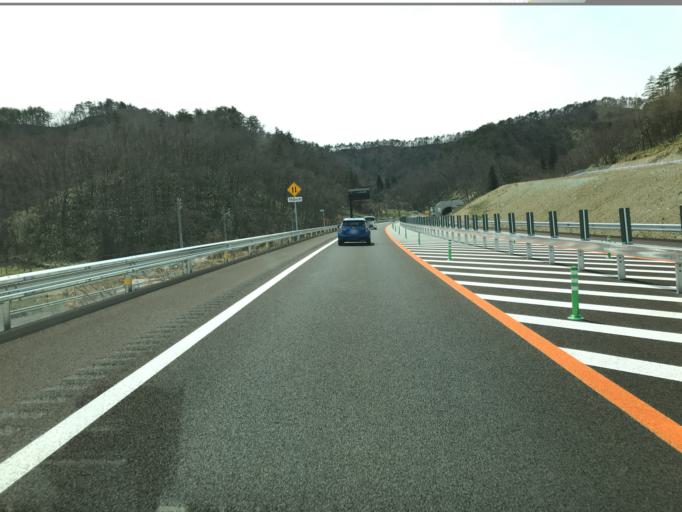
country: JP
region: Yamagata
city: Kaminoyama
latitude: 38.1165
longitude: 140.2473
